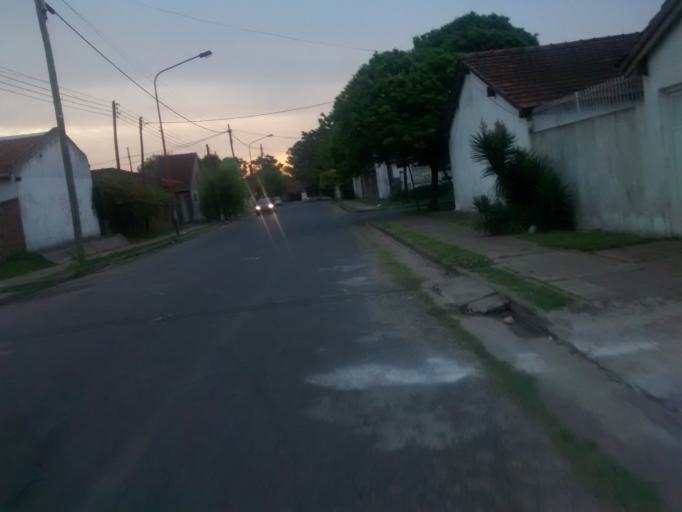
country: AR
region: Buenos Aires
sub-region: Partido de La Plata
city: La Plata
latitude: -34.9447
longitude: -57.9199
